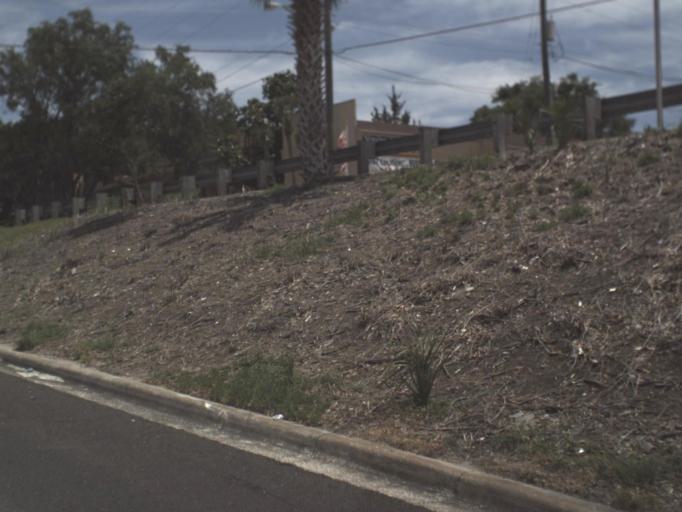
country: US
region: Florida
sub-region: Duval County
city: Jacksonville
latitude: 30.3274
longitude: -81.5960
